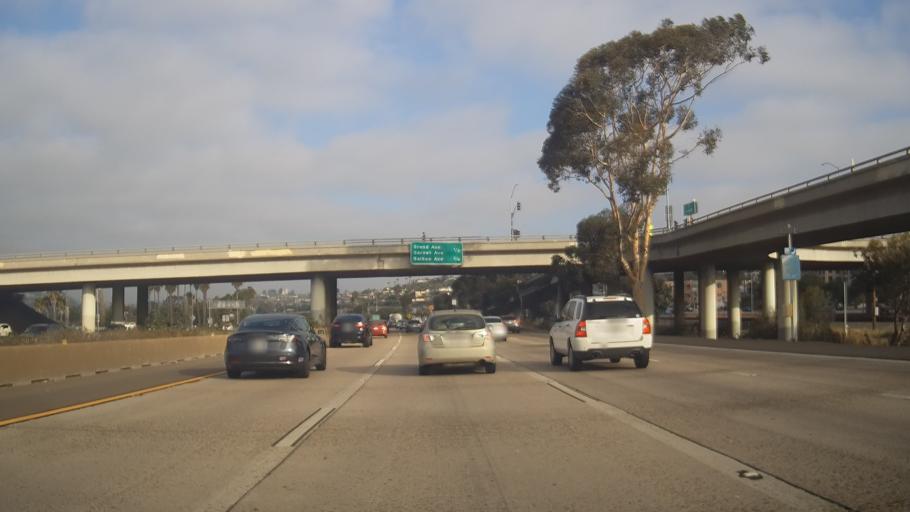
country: US
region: California
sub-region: San Diego County
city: La Jolla
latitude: 32.7898
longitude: -117.2069
